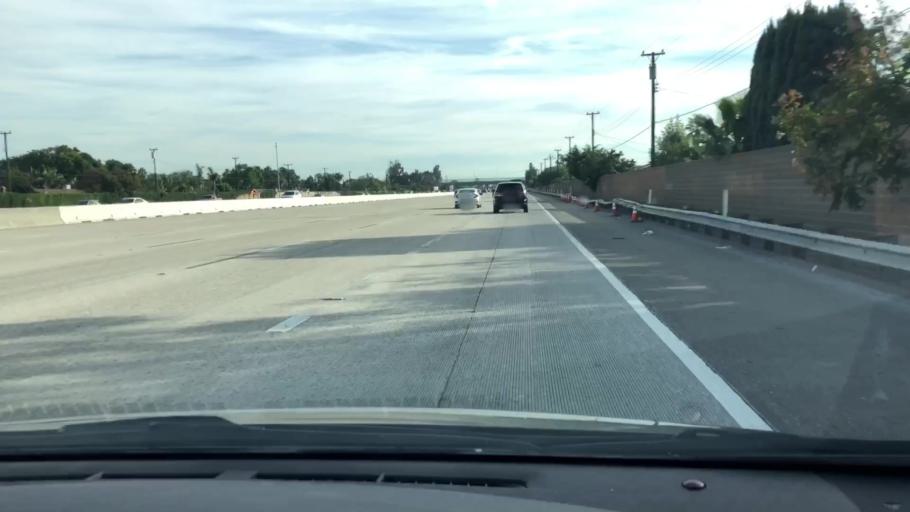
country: US
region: California
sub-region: Orange County
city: Anaheim
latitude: 33.8310
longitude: -117.8763
